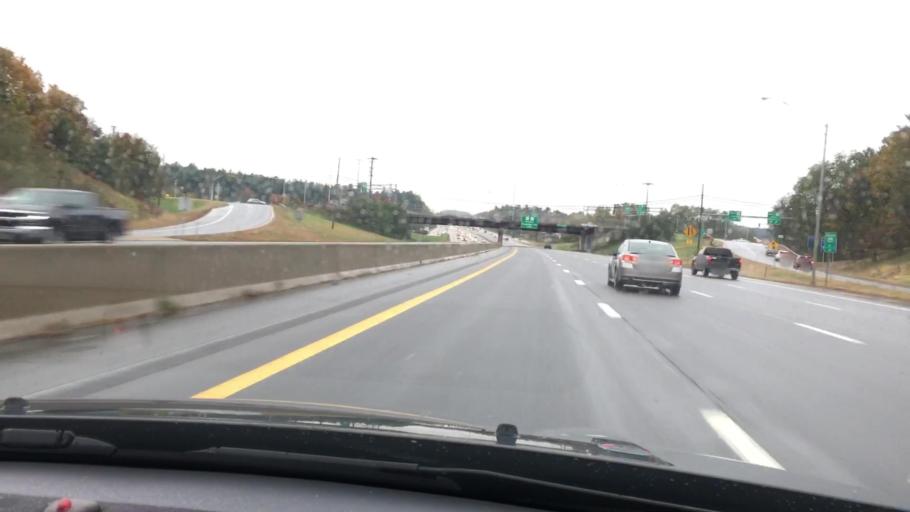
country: US
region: New Hampshire
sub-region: Hillsborough County
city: Nashua
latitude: 42.7713
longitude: -71.4933
